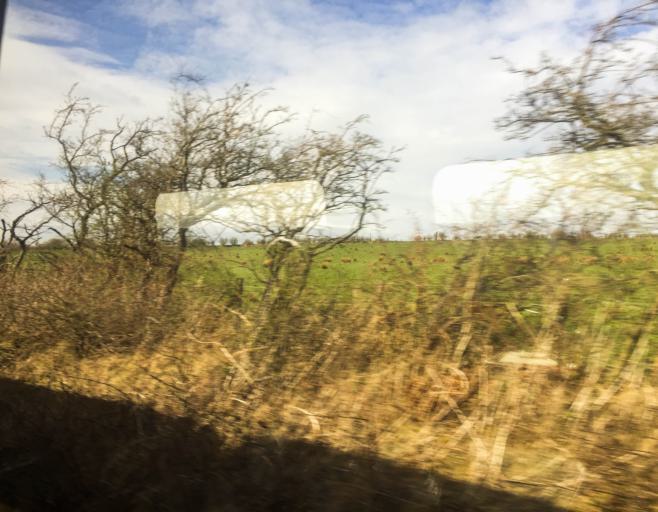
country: GB
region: Scotland
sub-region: North Lanarkshire
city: Chryston
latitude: 55.8890
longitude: -4.1006
